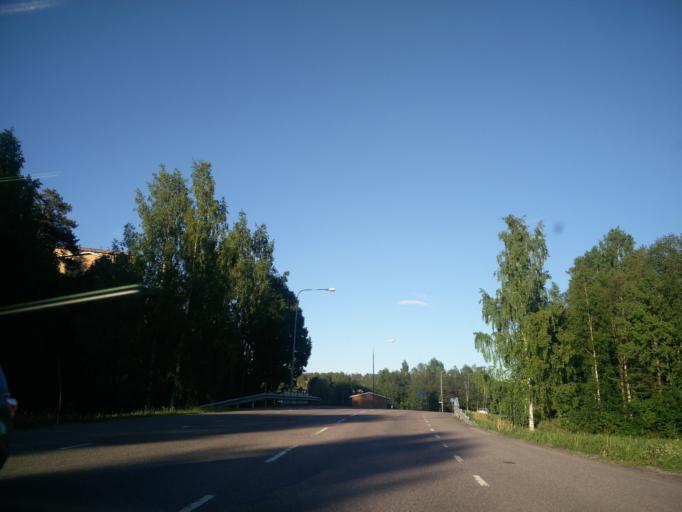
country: SE
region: Vaesternorrland
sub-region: Sundsvalls Kommun
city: Sundsvall
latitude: 62.4102
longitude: 17.2649
